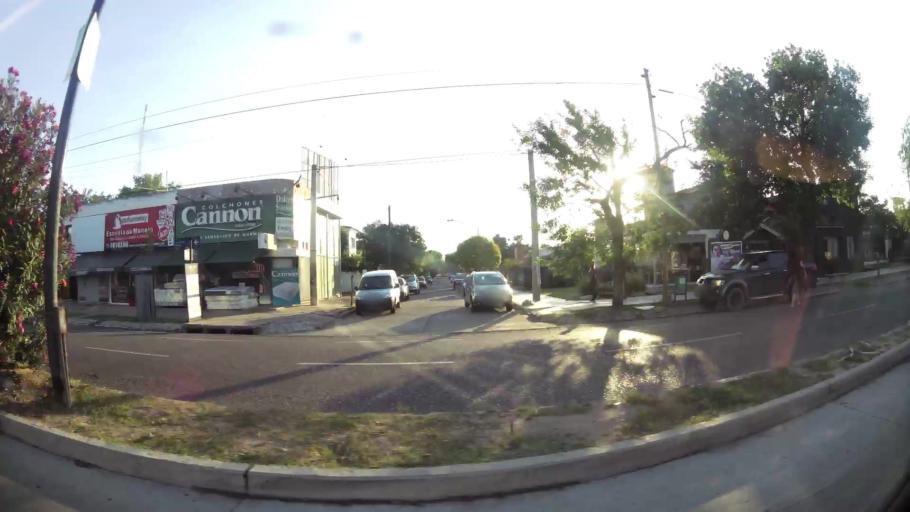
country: AR
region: Cordoba
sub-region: Departamento de Capital
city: Cordoba
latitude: -31.3777
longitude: -64.2251
